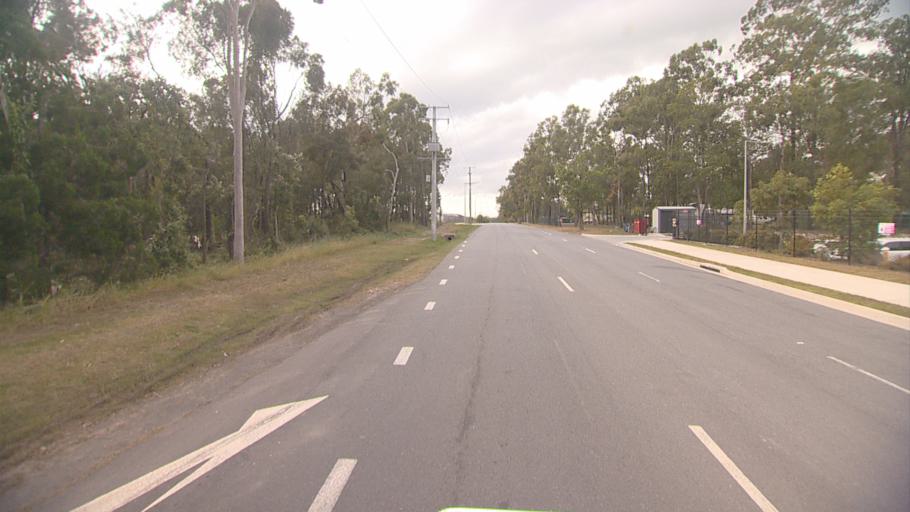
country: AU
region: Queensland
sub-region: Logan
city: Woodridge
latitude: -27.6518
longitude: 153.0892
